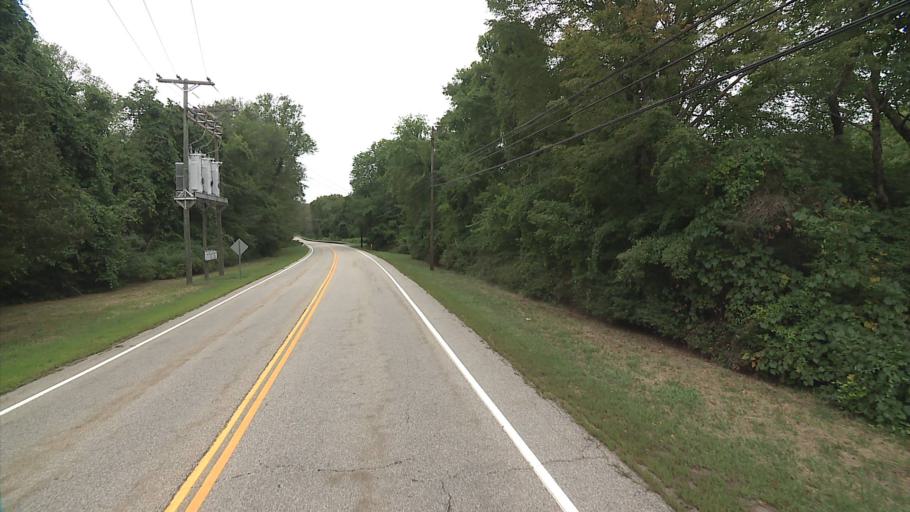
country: US
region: Connecticut
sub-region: Middlesex County
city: Essex Village
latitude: 41.4295
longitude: -72.3354
